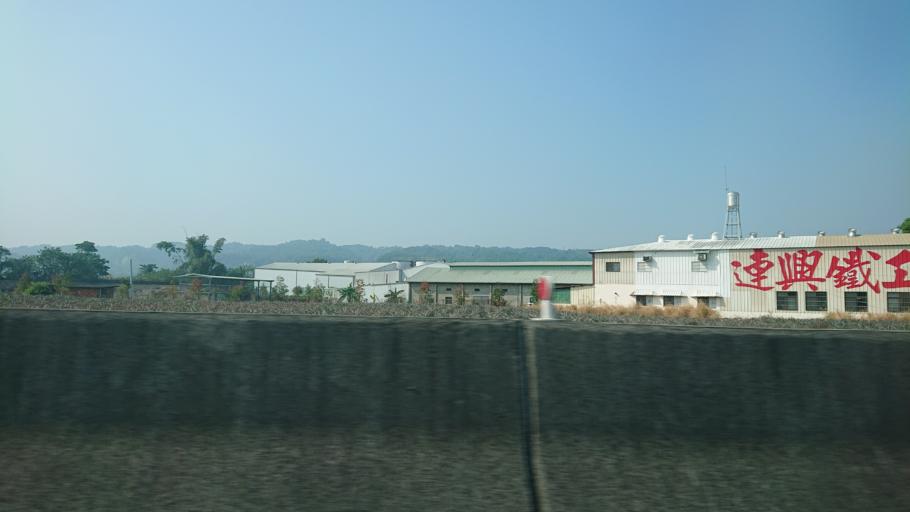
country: TW
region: Taiwan
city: Lugu
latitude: 23.7644
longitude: 120.6601
